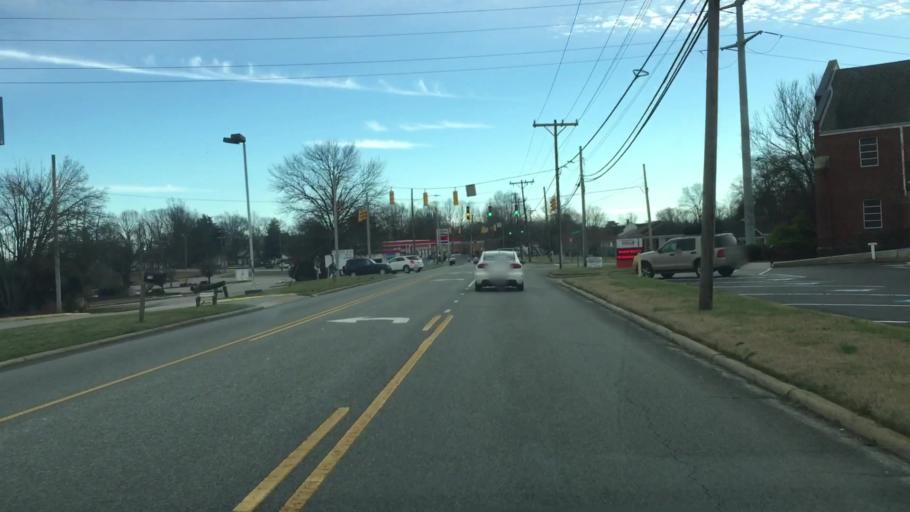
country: US
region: North Carolina
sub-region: Rockingham County
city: Reidsville
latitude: 36.3419
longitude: -79.6635
